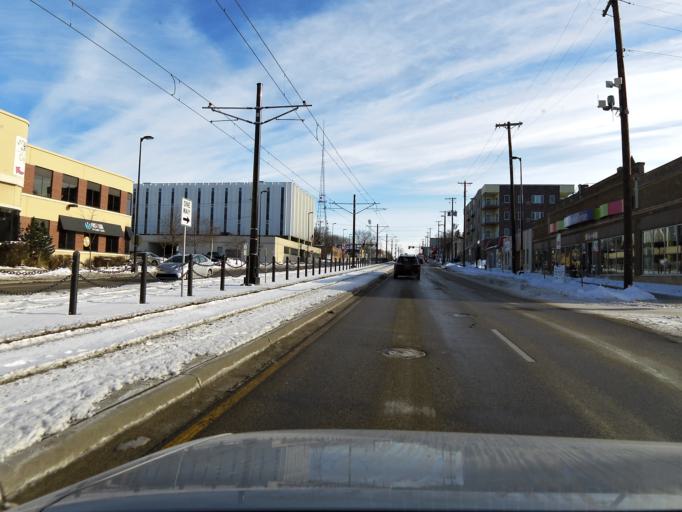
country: US
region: Minnesota
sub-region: Ramsey County
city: Lauderdale
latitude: 44.9707
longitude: -93.2149
